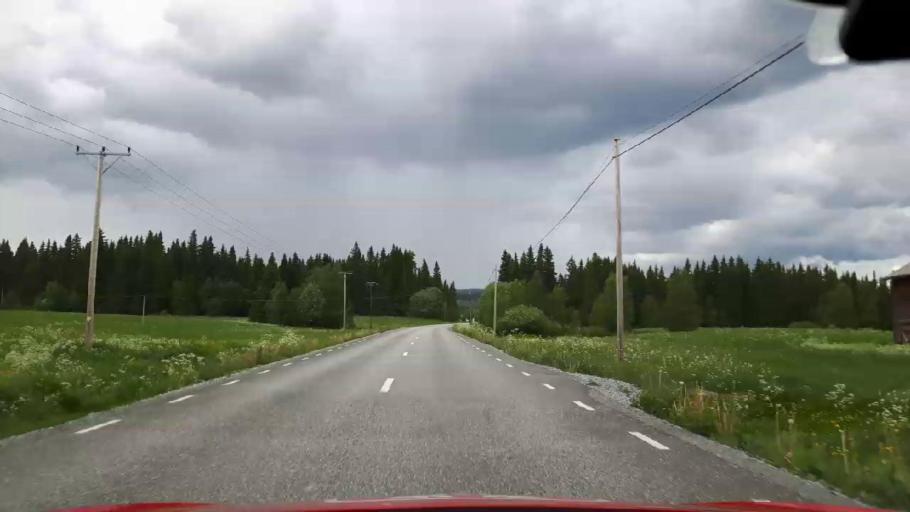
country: SE
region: Jaemtland
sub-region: Krokoms Kommun
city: Krokom
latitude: 63.6761
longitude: 14.3413
